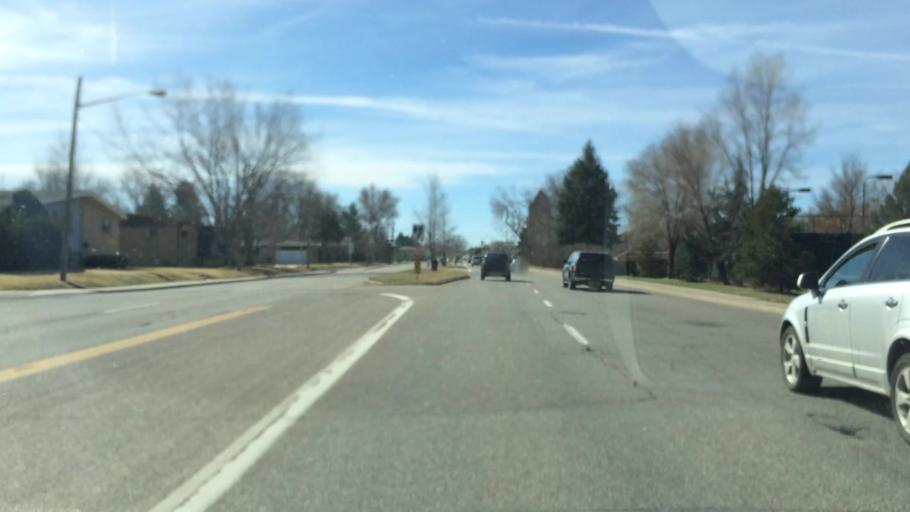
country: US
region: Colorado
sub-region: Arapahoe County
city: Glendale
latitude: 39.6839
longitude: -104.9129
